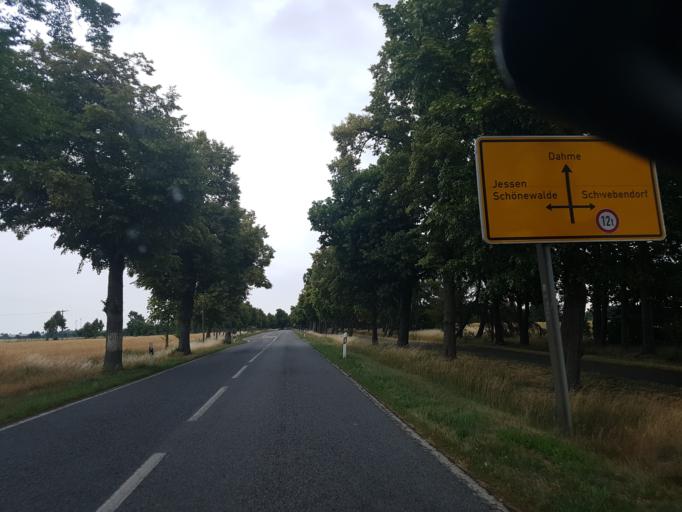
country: DE
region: Brandenburg
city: Dahme
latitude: 51.8555
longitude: 13.4143
